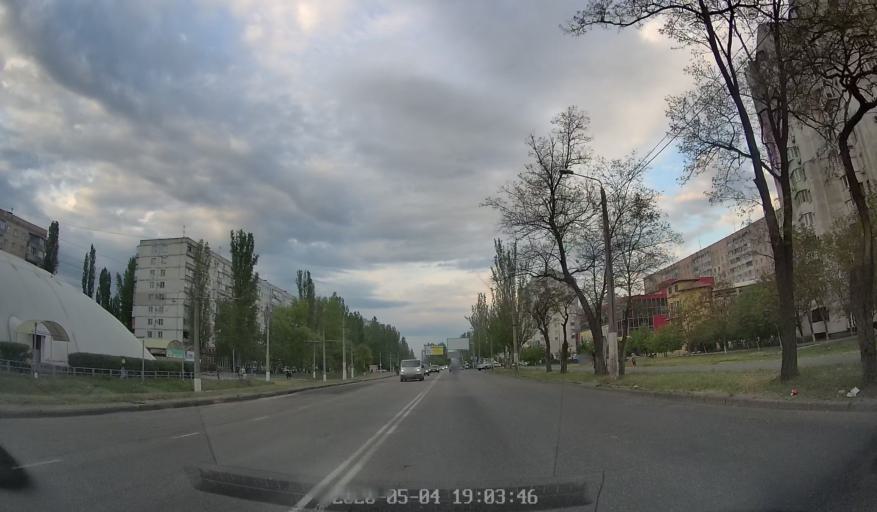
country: NG
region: Niger
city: Lemu
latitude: 9.3181
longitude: 6.1592
